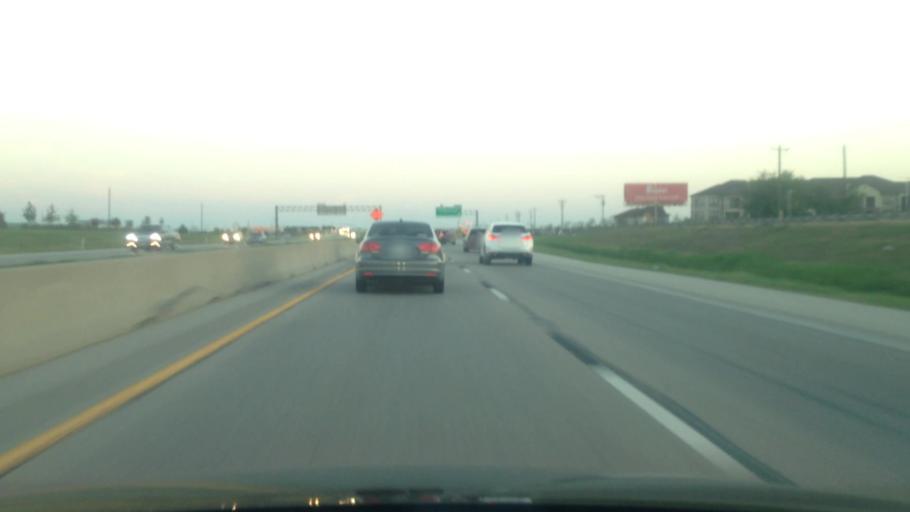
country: US
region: Texas
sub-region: Tarrant County
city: Haslet
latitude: 32.9238
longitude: -97.3172
